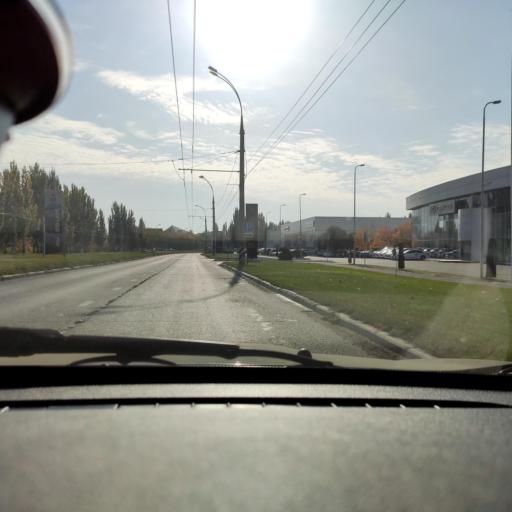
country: RU
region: Samara
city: Tol'yatti
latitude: 53.5455
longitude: 49.2763
